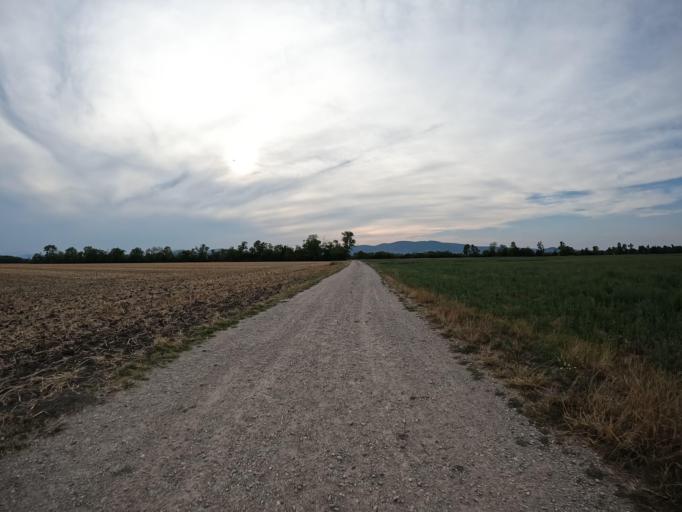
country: AT
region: Lower Austria
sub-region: Politischer Bezirk Baden
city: Trumau
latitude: 48.0028
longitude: 16.3372
